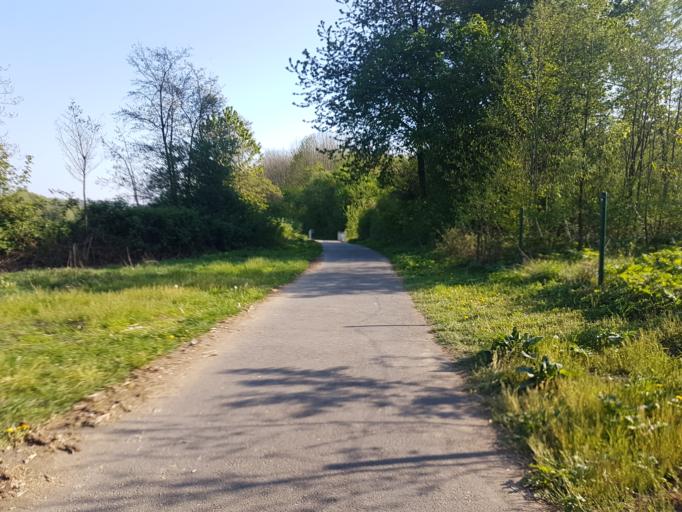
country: DE
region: North Rhine-Westphalia
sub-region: Regierungsbezirk Dusseldorf
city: Essen
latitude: 51.4380
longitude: 7.0839
